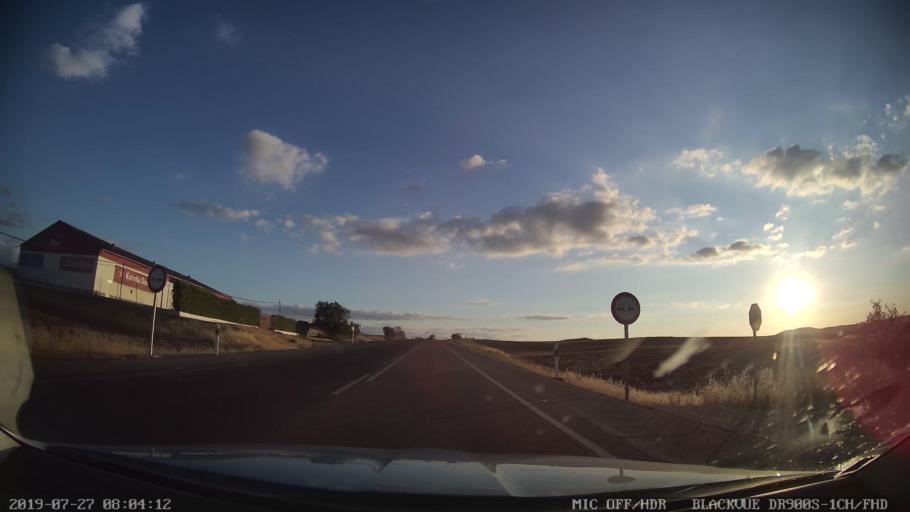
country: ES
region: Extremadura
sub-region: Provincia de Badajoz
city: Merida
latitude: 38.9338
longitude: -6.3122
